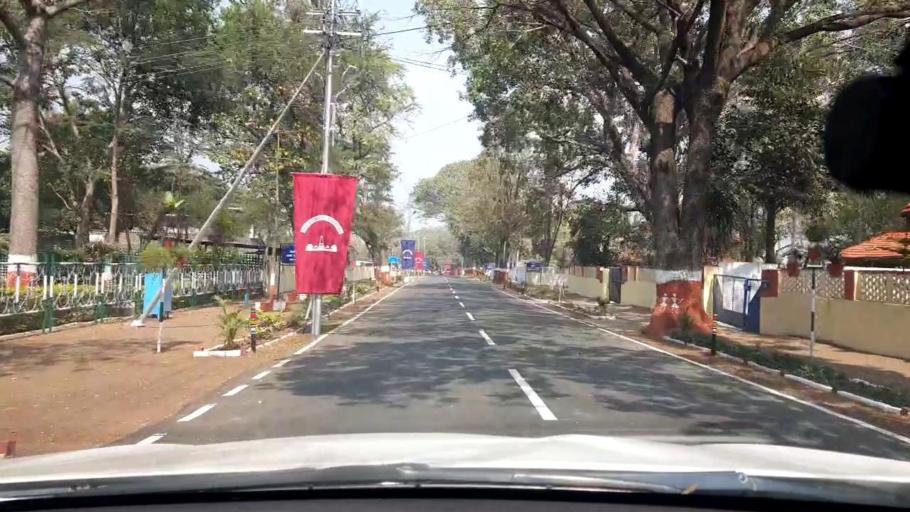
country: IN
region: Maharashtra
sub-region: Pune Division
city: Khadki
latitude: 18.5486
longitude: 73.8668
